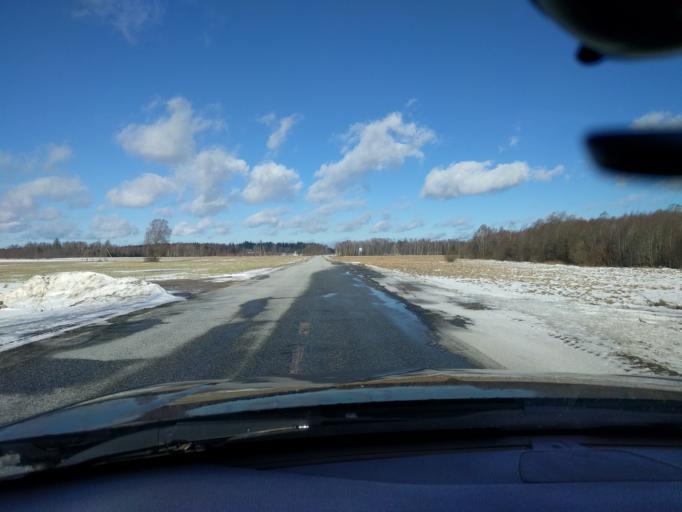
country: EE
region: Harju
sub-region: Raasiku vald
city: Raasiku
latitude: 59.3092
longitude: 25.1658
